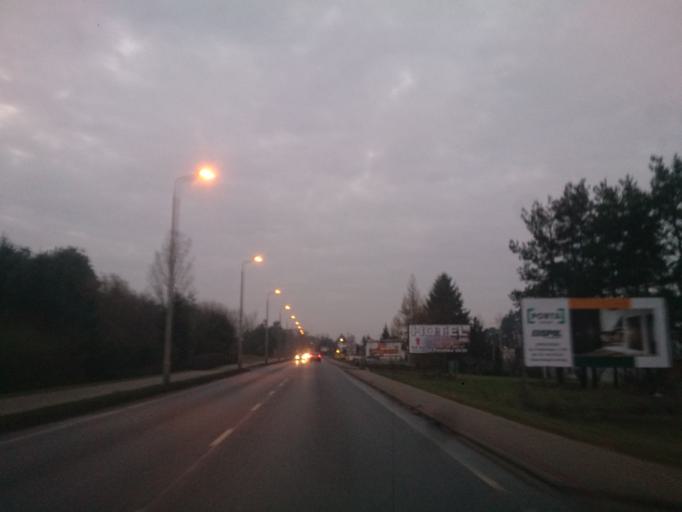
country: PL
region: Kujawsko-Pomorskie
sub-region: Grudziadz
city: Grudziadz
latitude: 53.4553
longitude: 18.7892
